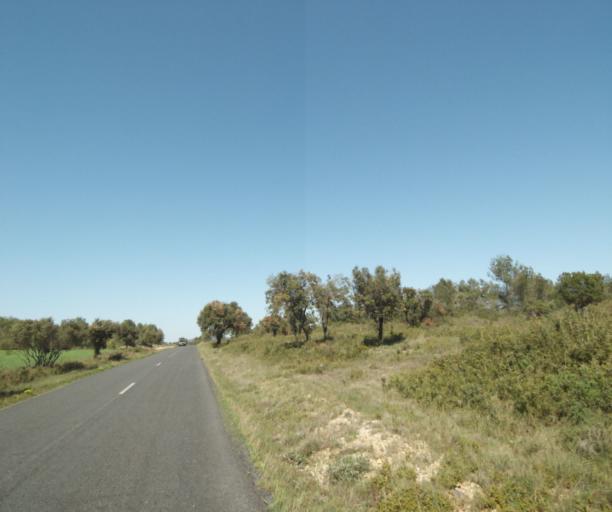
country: FR
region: Languedoc-Roussillon
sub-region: Departement de l'Herault
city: Saint-Drezery
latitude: 43.7318
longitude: 3.9567
